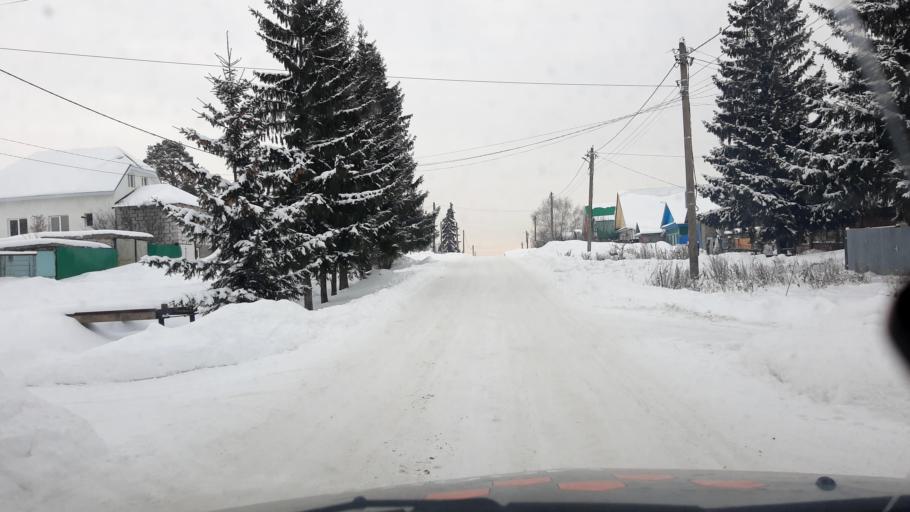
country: RU
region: Bashkortostan
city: Avdon
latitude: 54.7357
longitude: 55.7922
